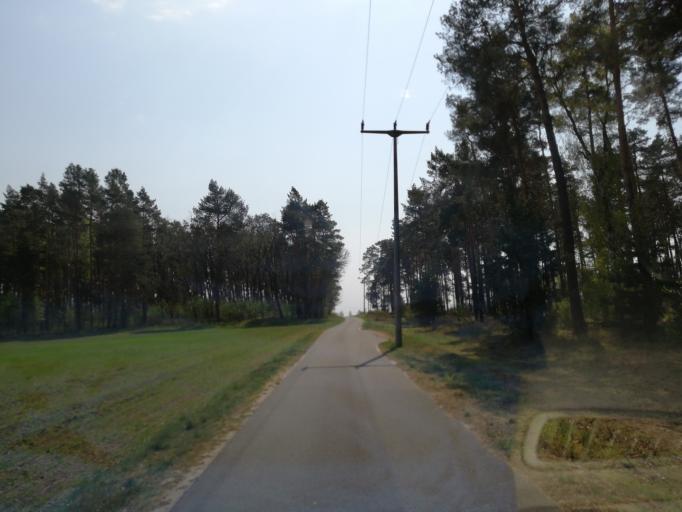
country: DE
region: Brandenburg
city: Bronkow
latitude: 51.6533
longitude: 13.8554
